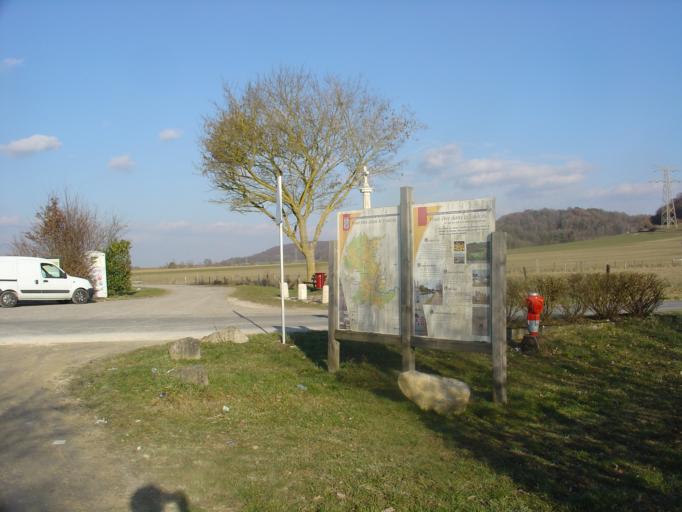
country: FR
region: Lorraine
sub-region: Departement de Meurthe-et-Moselle
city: Foug
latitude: 48.7135
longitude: 5.7763
